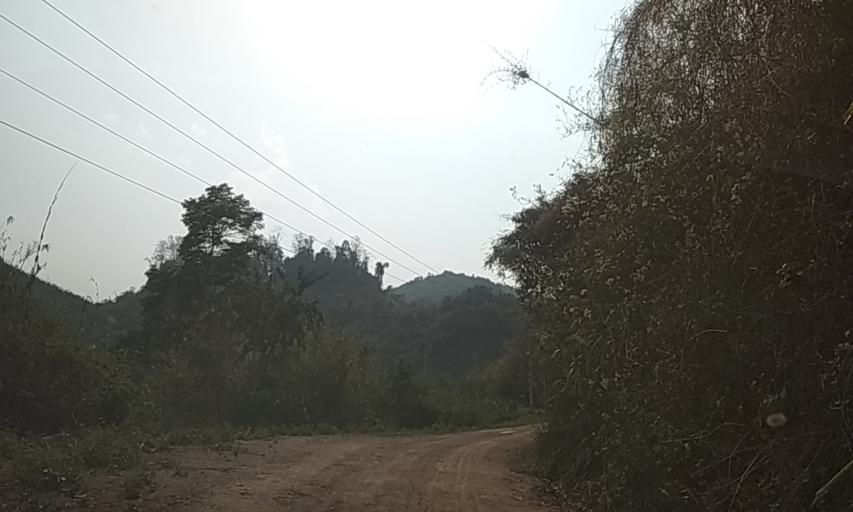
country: LA
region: Louangphabang
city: Louangphabang
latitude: 20.0458
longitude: 101.8430
